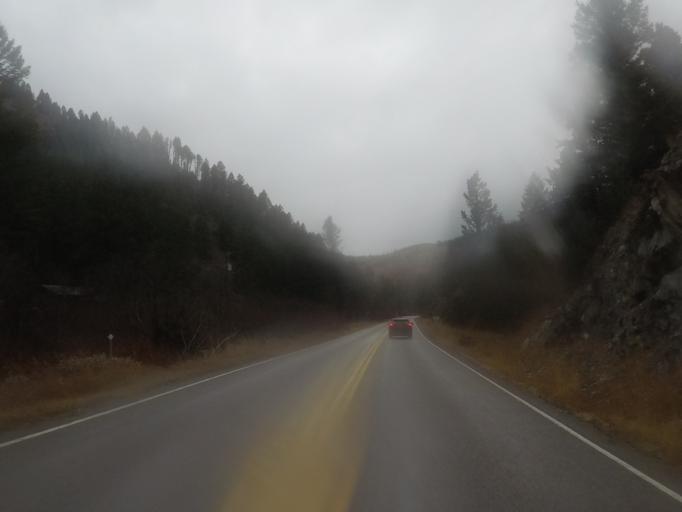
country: US
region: Montana
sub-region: Broadwater County
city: Townsend
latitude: 46.3308
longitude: -111.2077
